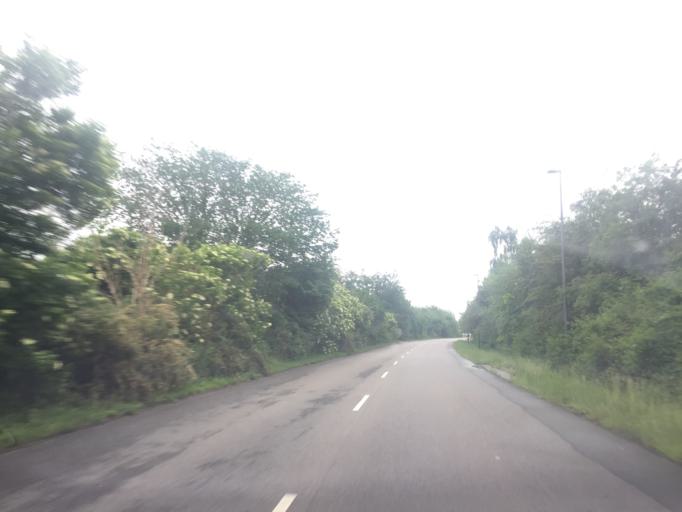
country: DK
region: Capital Region
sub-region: Glostrup Kommune
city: Glostrup
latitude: 55.6776
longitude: 12.3827
